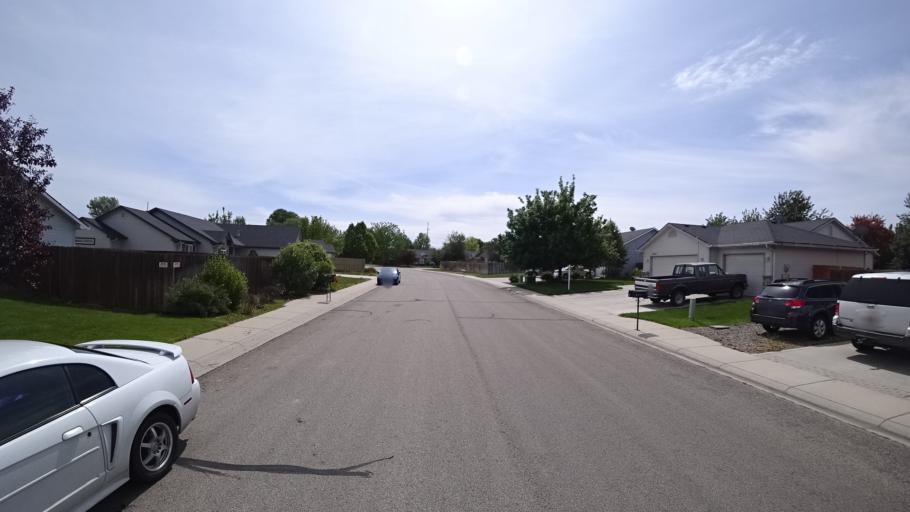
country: US
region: Idaho
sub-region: Ada County
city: Meridian
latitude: 43.5551
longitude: -116.3362
